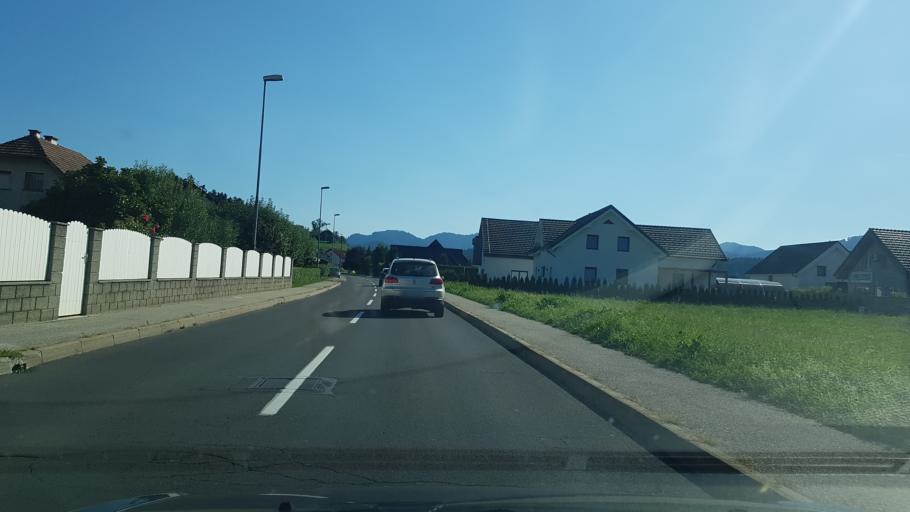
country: SI
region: Slovenj Gradec
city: Slovenj Gradec
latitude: 46.5028
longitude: 15.0741
